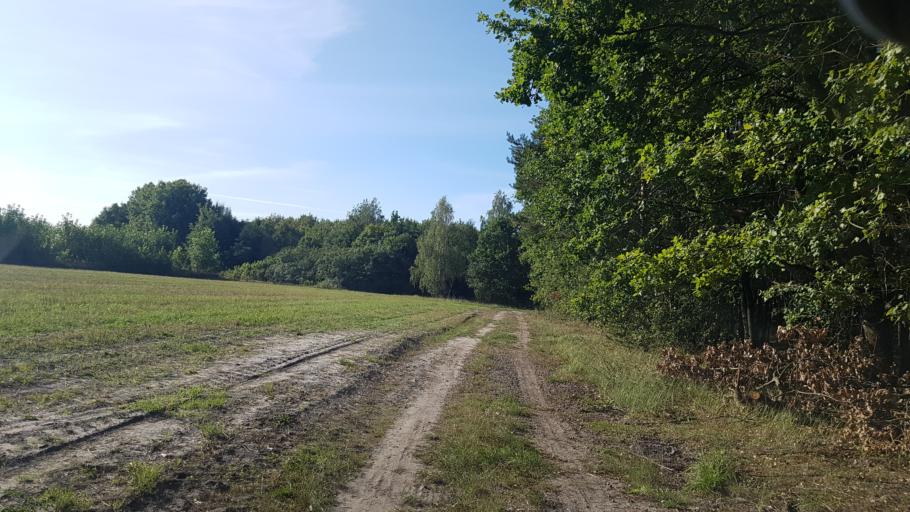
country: DE
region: Brandenburg
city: Finsterwalde
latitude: 51.5789
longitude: 13.6536
